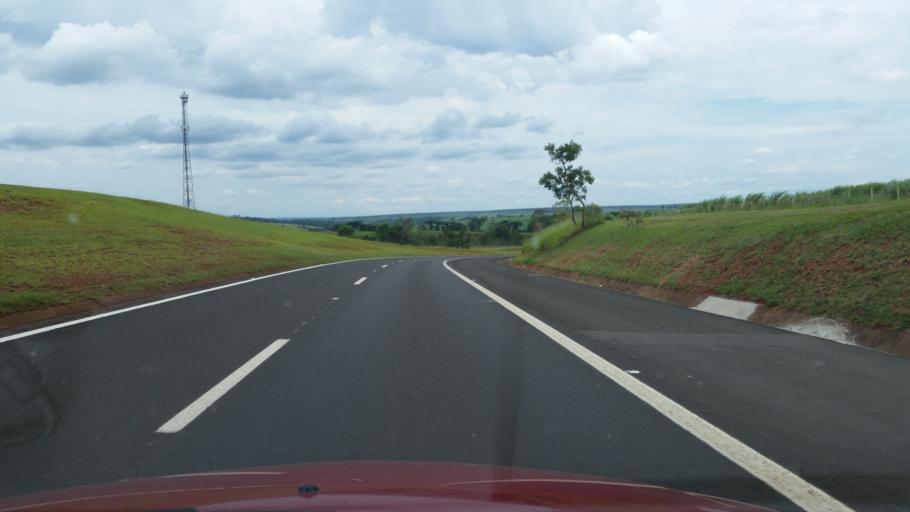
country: BR
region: Sao Paulo
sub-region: Avare
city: Avare
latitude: -22.9663
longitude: -48.8057
